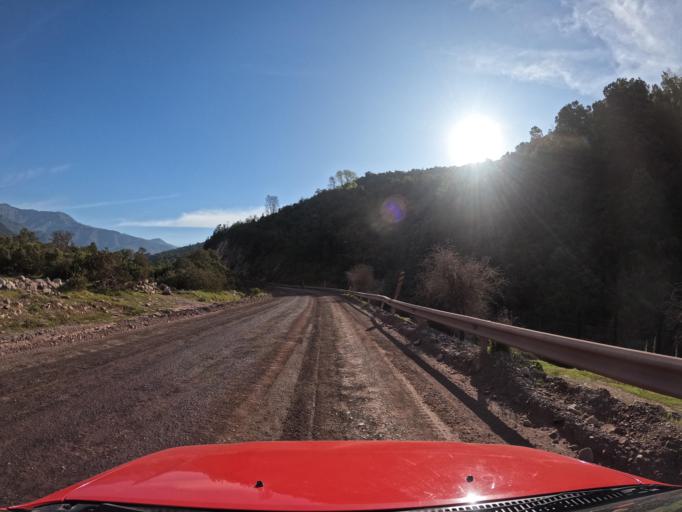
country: CL
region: O'Higgins
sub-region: Provincia de Colchagua
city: Chimbarongo
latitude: -34.9954
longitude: -70.8196
